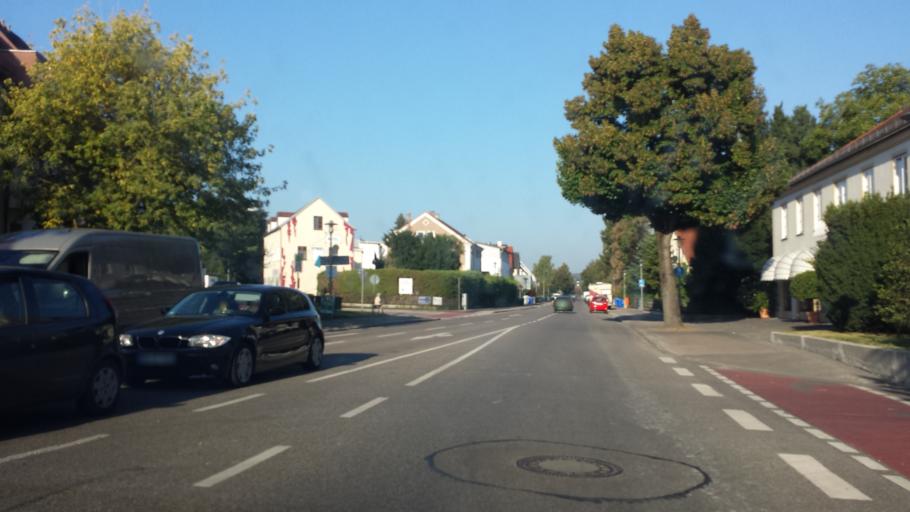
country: DE
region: Bavaria
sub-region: Upper Bavaria
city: Neuburg an der Donau
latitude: 48.7404
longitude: 11.1813
